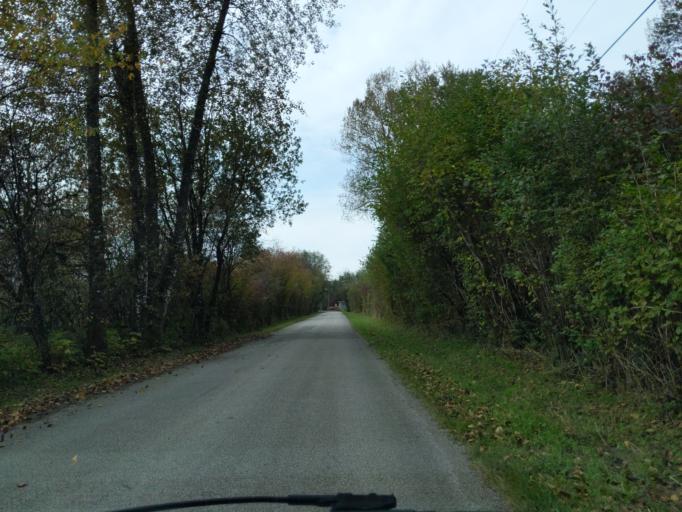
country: CA
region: British Columbia
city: Walnut Grove
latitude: 49.1965
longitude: -122.6486
